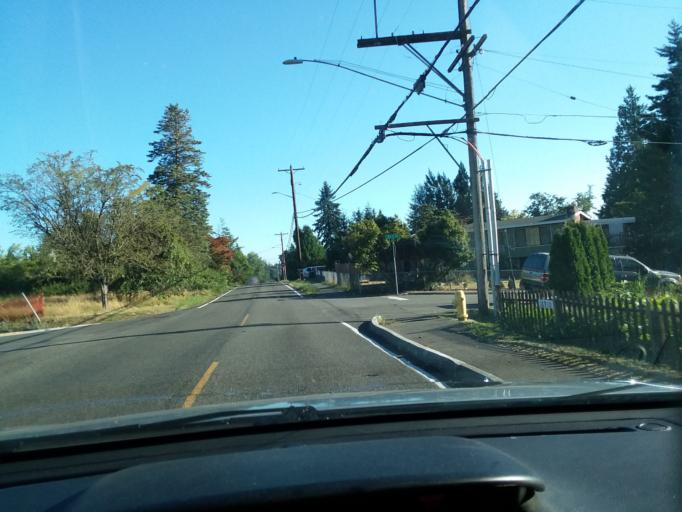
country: US
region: Washington
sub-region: Snohomish County
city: Alderwood Manor
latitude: 47.8270
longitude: -122.2871
